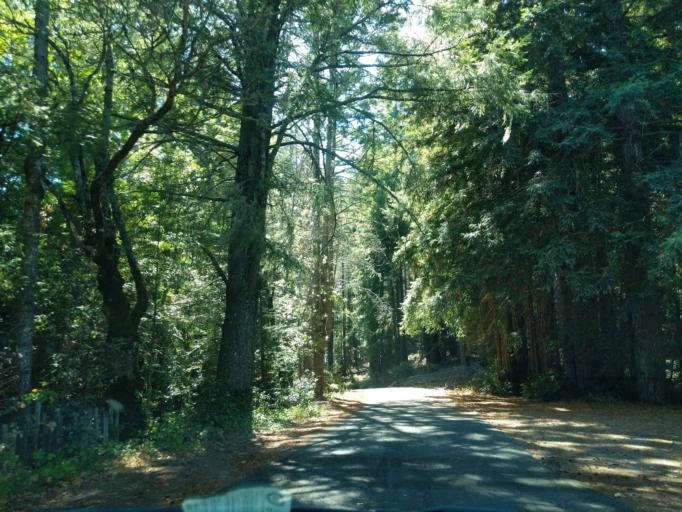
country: US
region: California
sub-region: Sonoma County
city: Monte Rio
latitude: 38.5272
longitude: -123.2272
